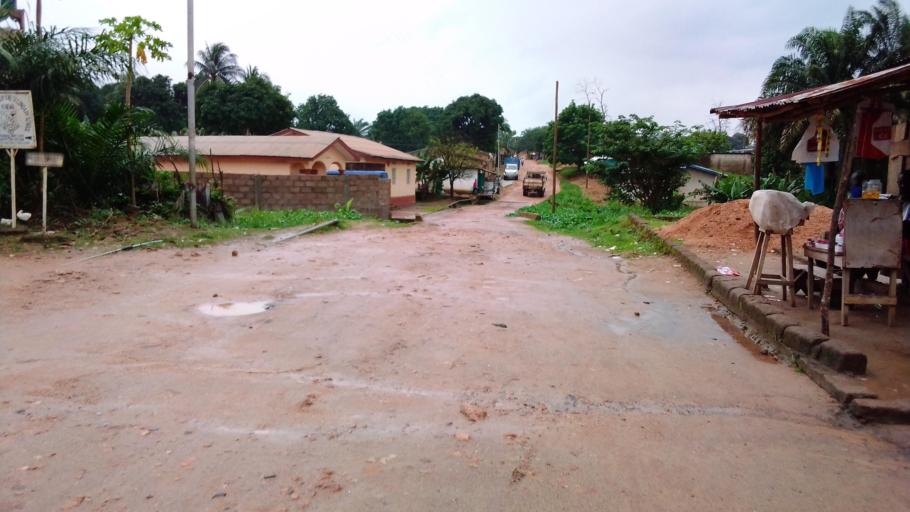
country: SL
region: Eastern Province
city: Kenema
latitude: 7.8938
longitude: -11.1873
